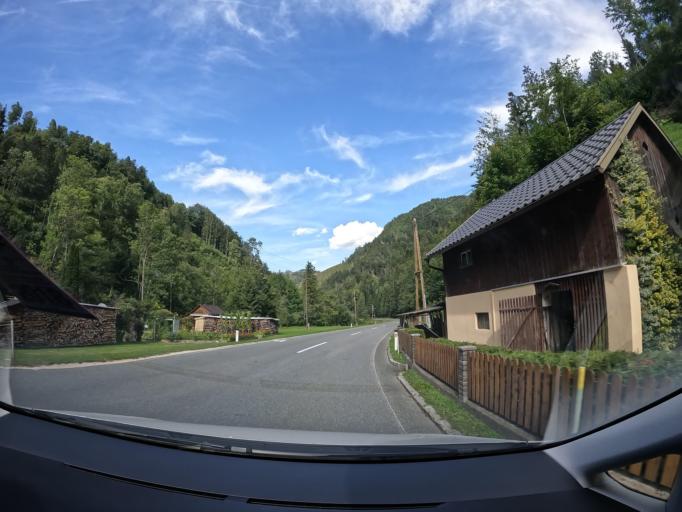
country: AT
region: Carinthia
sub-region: Politischer Bezirk Volkermarkt
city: Bad Eisenkappel
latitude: 46.4534
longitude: 14.5817
